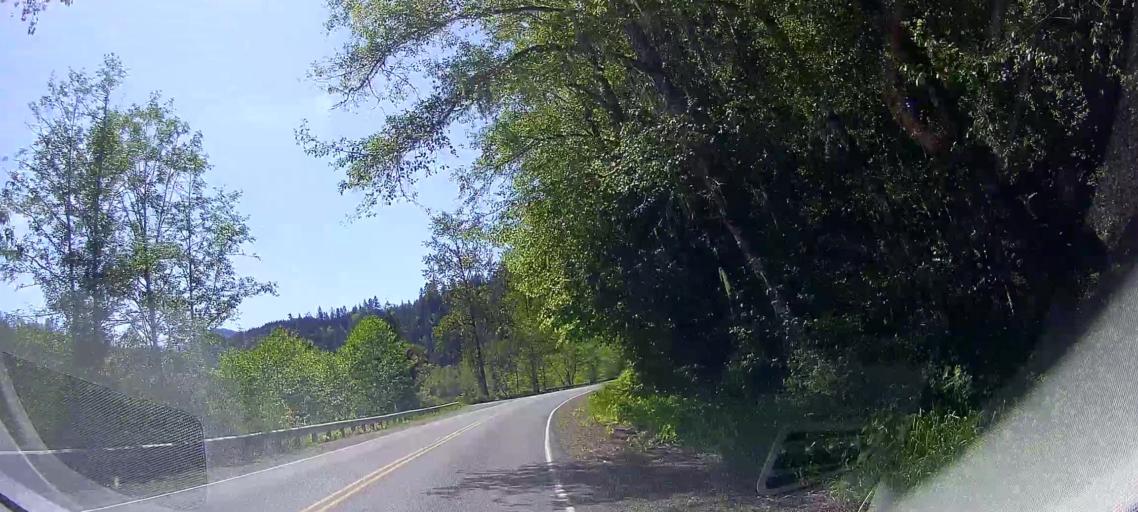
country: US
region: Washington
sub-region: Snohomish County
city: Darrington
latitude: 48.5092
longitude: -121.7226
